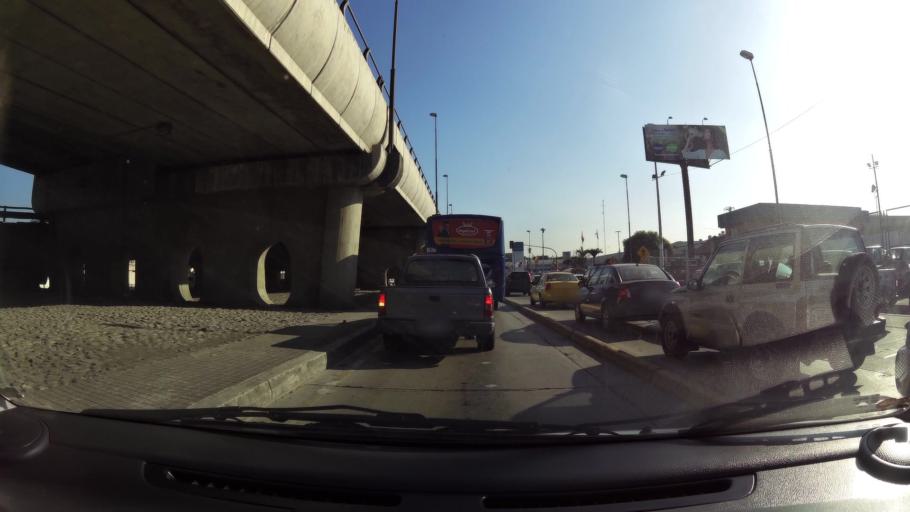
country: EC
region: Guayas
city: Eloy Alfaro
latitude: -2.1713
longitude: -79.8794
